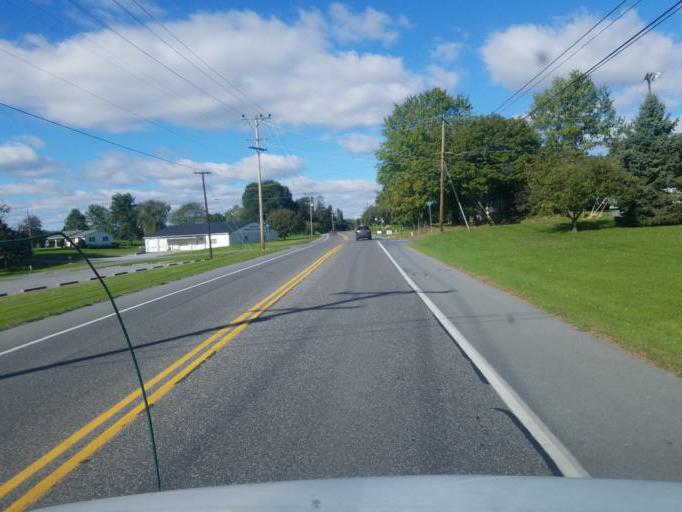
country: US
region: Pennsylvania
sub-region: Franklin County
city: Greencastle
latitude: 39.8009
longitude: -77.7892
